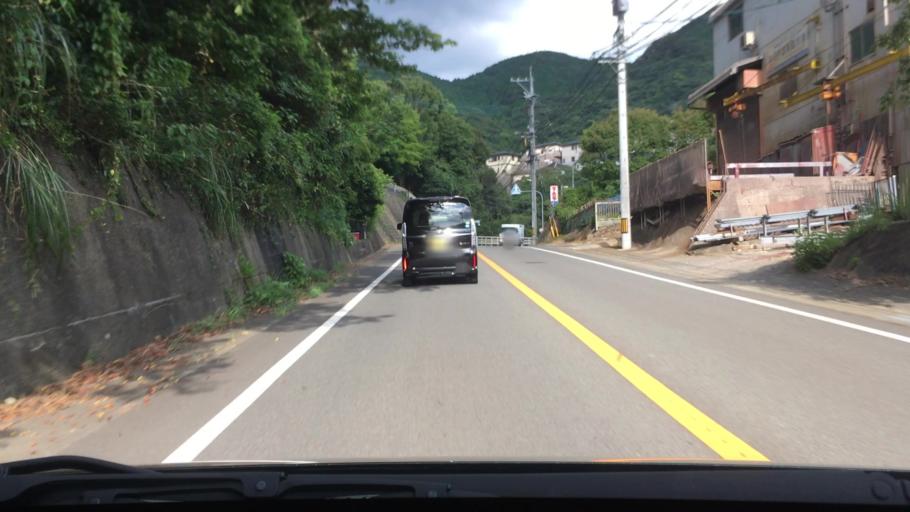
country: JP
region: Nagasaki
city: Togitsu
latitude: 32.8173
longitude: 129.8064
